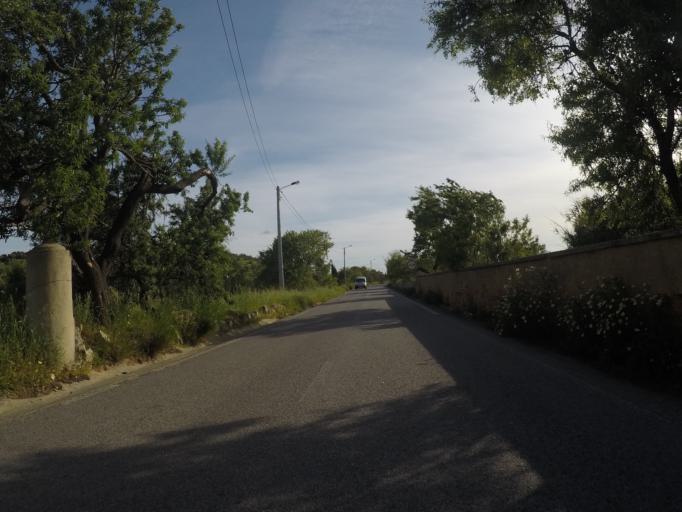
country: PT
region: Faro
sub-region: Lagos
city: Lagos
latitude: 37.1036
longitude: -8.7115
